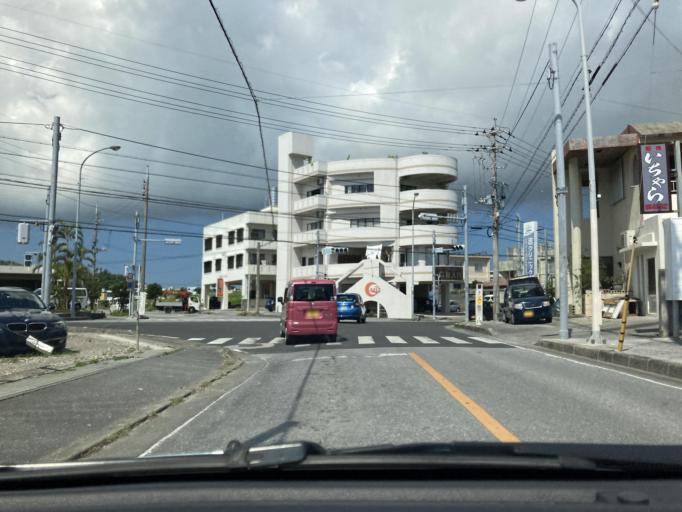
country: JP
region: Okinawa
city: Tomigusuku
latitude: 26.1758
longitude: 127.7191
